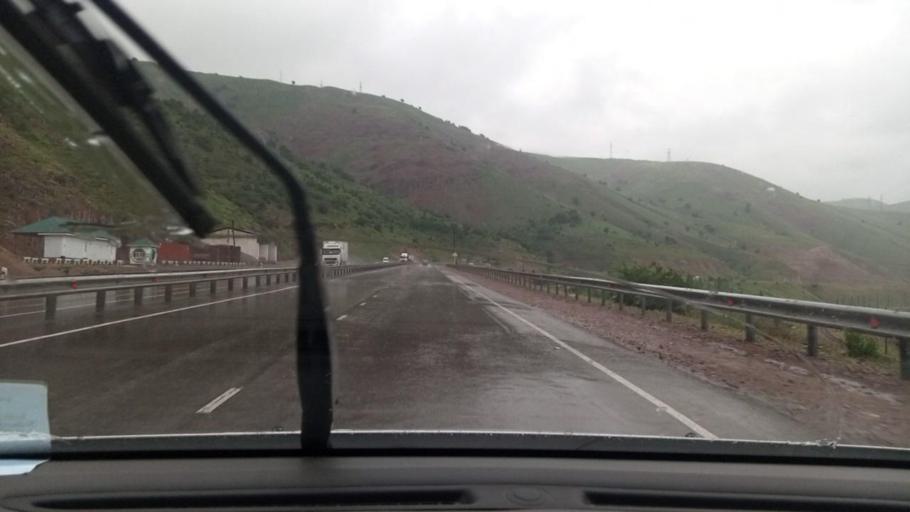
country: UZ
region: Toshkent
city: Angren
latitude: 41.0888
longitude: 70.3214
